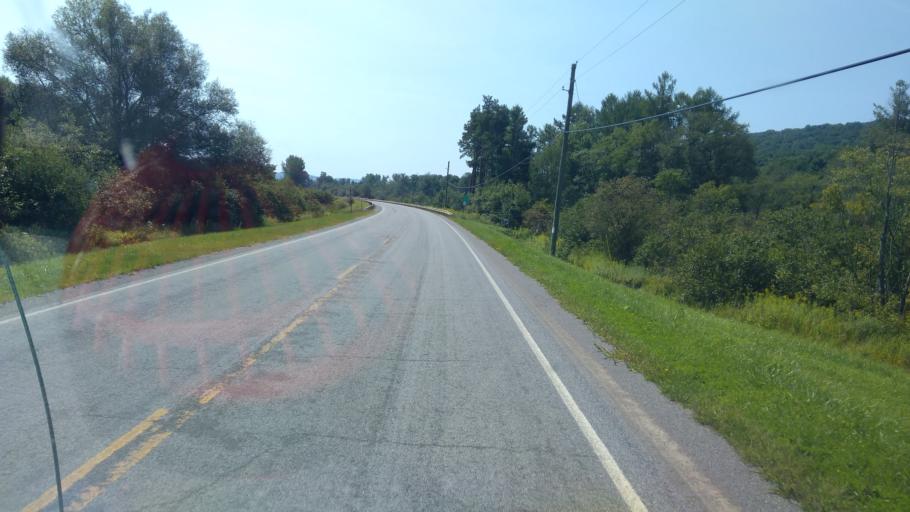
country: US
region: New York
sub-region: Allegany County
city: Alfred
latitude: 42.3493
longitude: -77.9248
